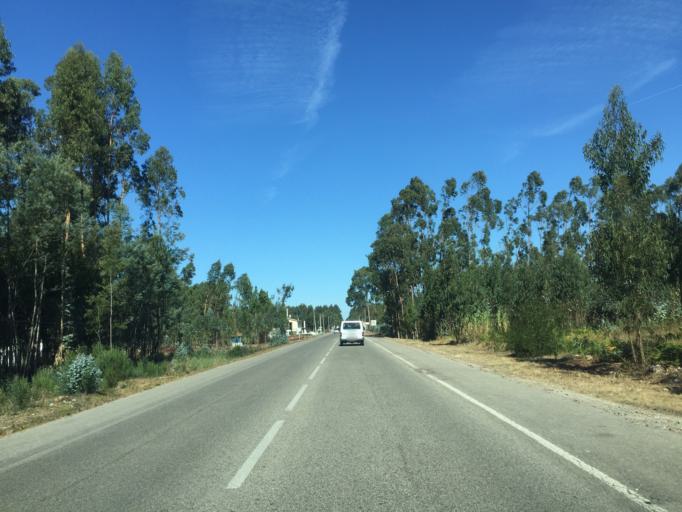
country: PT
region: Coimbra
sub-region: Figueira da Foz
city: Alhadas
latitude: 40.2886
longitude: -8.7670
